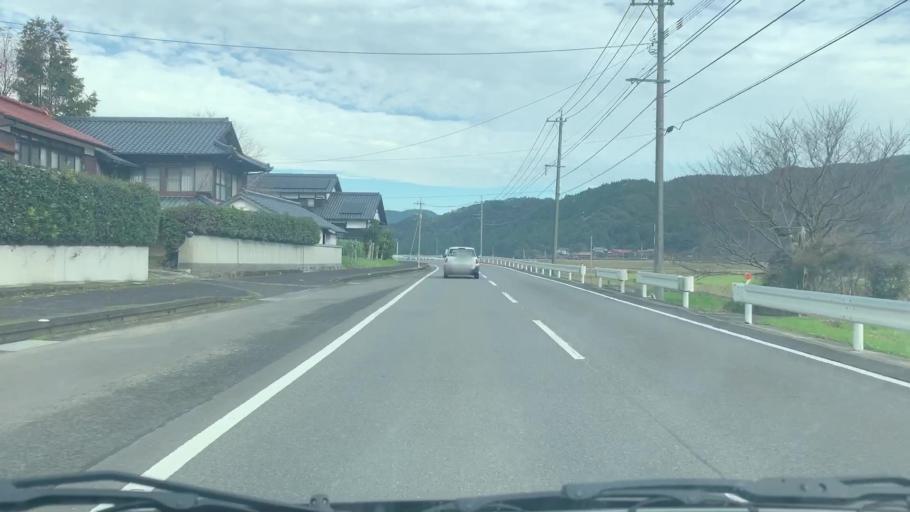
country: JP
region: Saga Prefecture
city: Imaricho-ko
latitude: 33.3115
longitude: 129.9713
